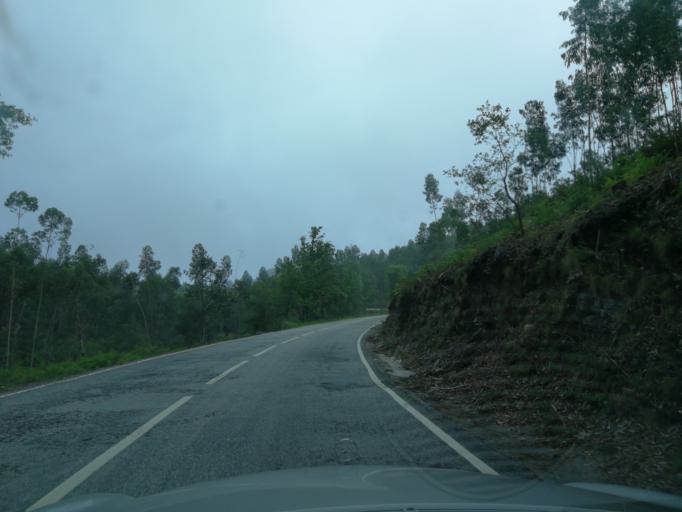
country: PT
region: Braga
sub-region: Braga
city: Braga
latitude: 41.5197
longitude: -8.3801
